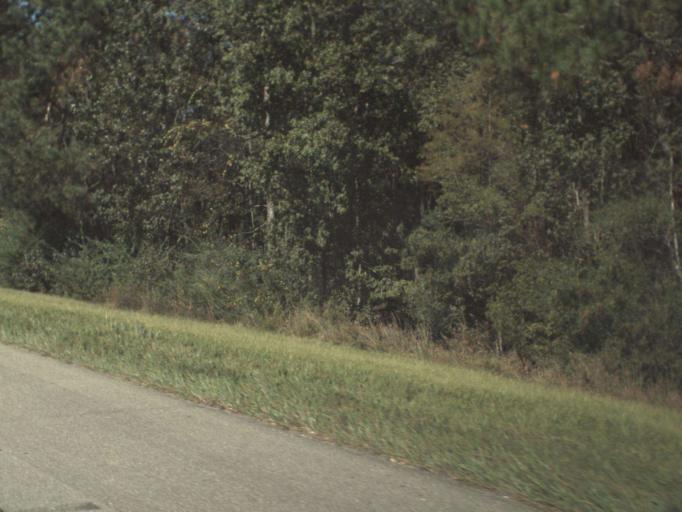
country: US
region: Florida
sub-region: Washington County
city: Chipley
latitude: 30.7458
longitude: -85.4454
